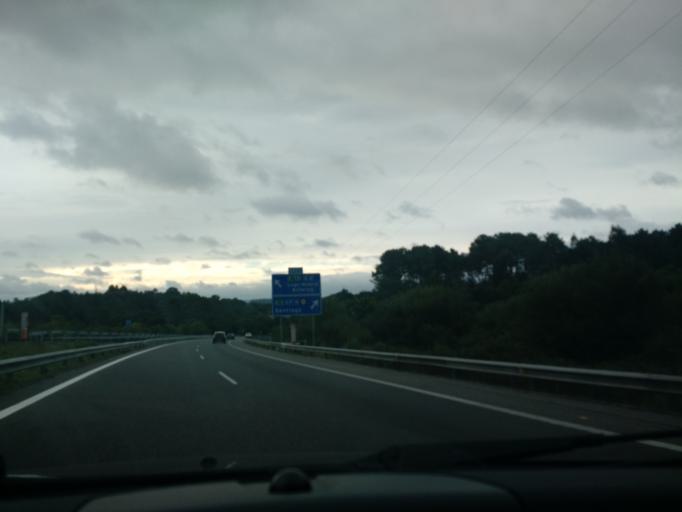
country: ES
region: Galicia
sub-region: Provincia da Coruna
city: Bergondo
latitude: 43.2873
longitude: -8.2810
